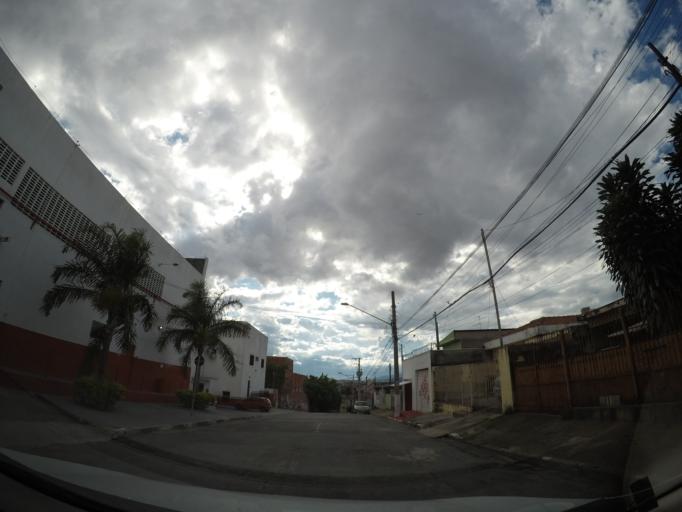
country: BR
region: Sao Paulo
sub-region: Guarulhos
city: Guarulhos
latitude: -23.4806
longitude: -46.5535
